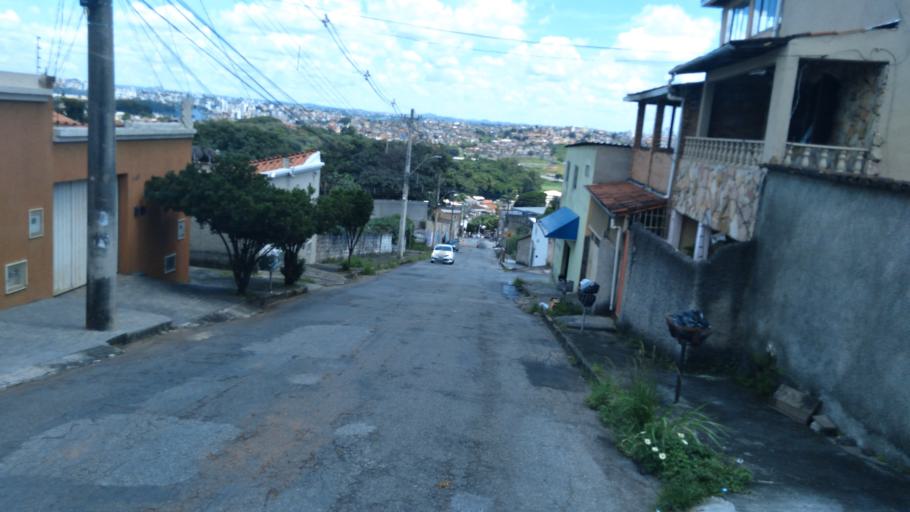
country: BR
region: Minas Gerais
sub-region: Belo Horizonte
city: Belo Horizonte
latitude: -19.8672
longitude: -43.9171
